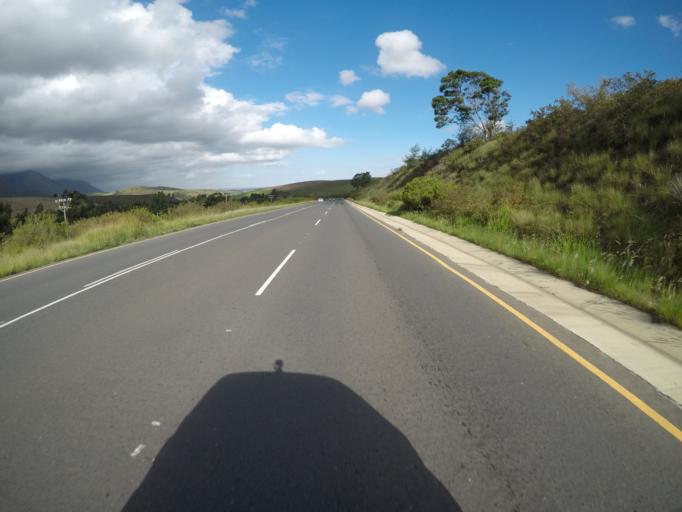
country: ZA
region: Western Cape
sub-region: Overberg District Municipality
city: Swellendam
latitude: -33.9964
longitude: 20.3554
